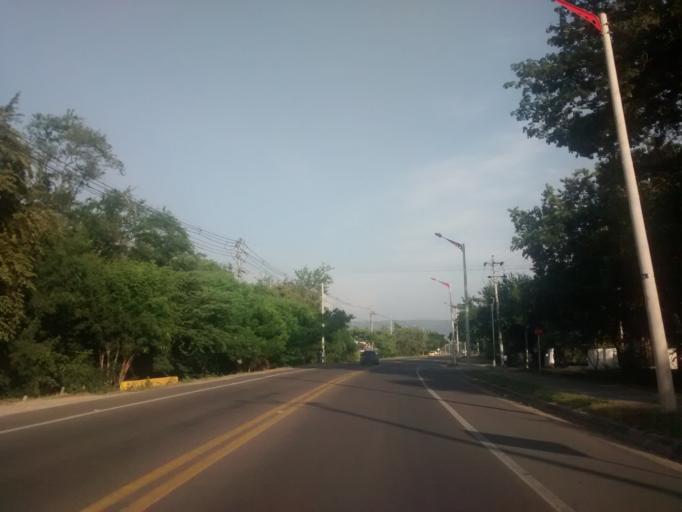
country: CO
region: Cundinamarca
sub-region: Girardot
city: Girardot City
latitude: 4.2949
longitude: -74.7860
